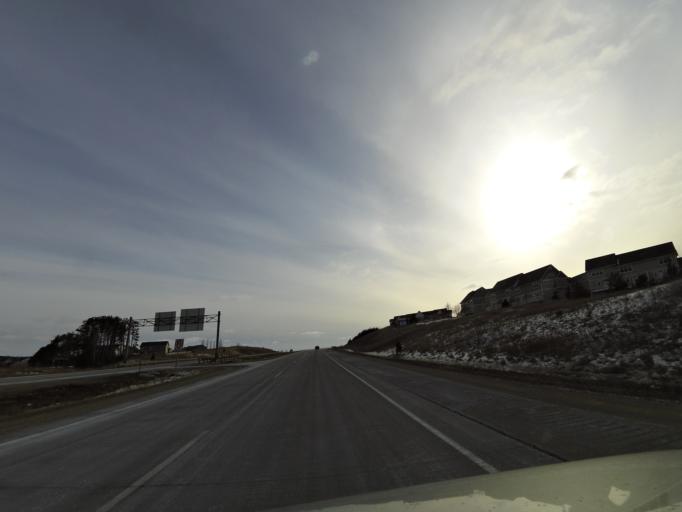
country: US
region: Wisconsin
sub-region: Saint Croix County
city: Hudson
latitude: 44.9569
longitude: -92.6949
